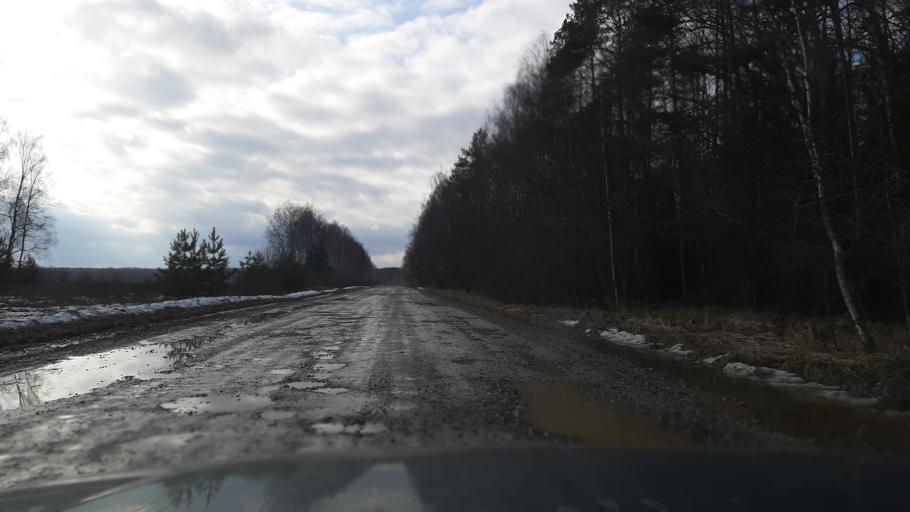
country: RU
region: Ivanovo
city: Teykovo
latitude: 56.8845
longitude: 40.6401
